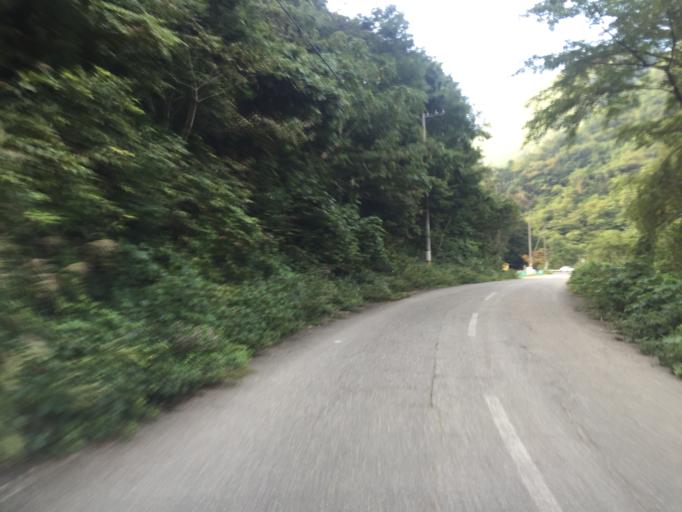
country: JP
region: Fukushima
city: Inawashiro
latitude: 37.4428
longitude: 139.9702
